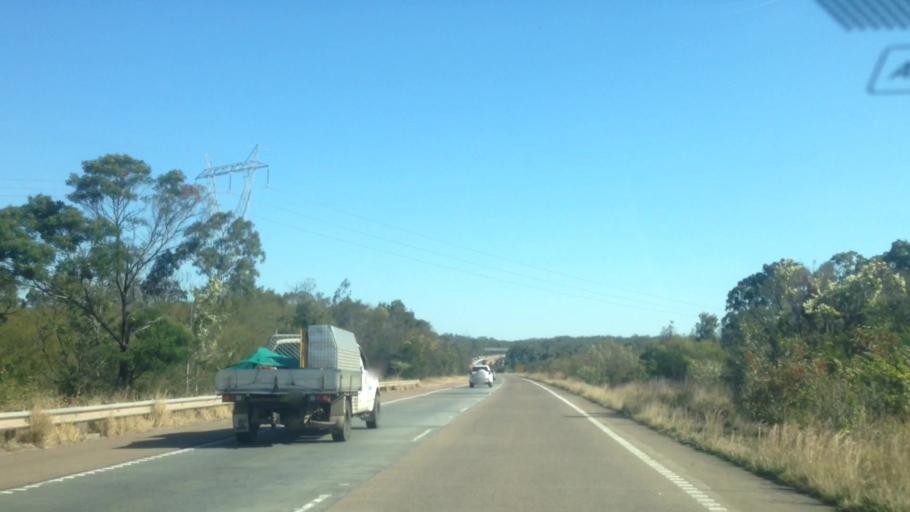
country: AU
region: New South Wales
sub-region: Wyong Shire
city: Jilliby
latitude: -33.2061
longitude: 151.4570
